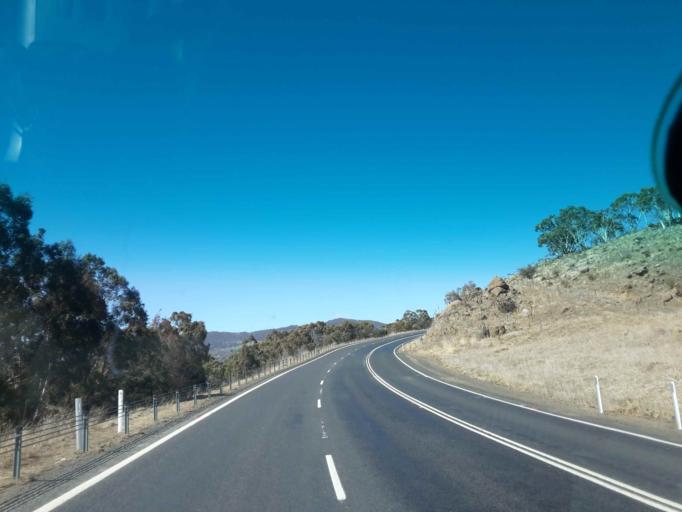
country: AU
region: New South Wales
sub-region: Snowy River
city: Jindabyne
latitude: -36.4122
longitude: 148.6021
